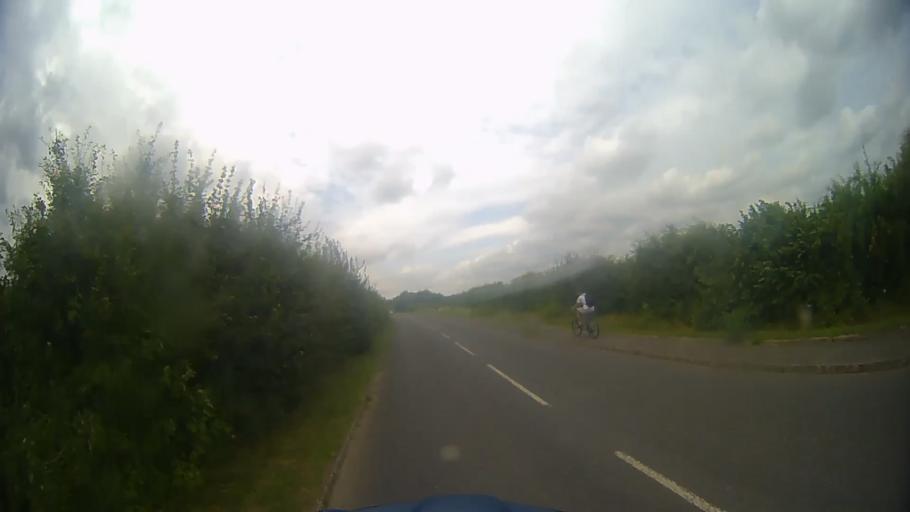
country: GB
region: England
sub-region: Hampshire
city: Kingsley
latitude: 51.1837
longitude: -0.8773
